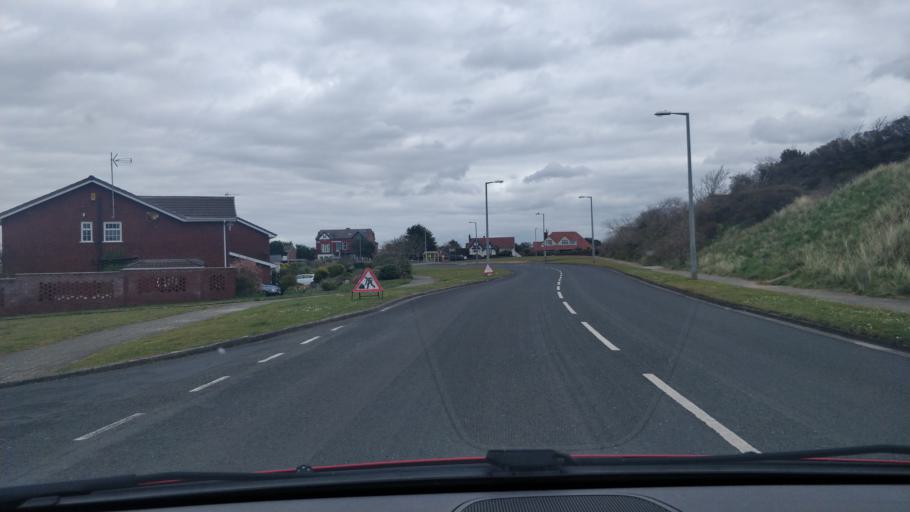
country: GB
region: England
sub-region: Sefton
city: Formby
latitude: 53.6026
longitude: -3.0497
